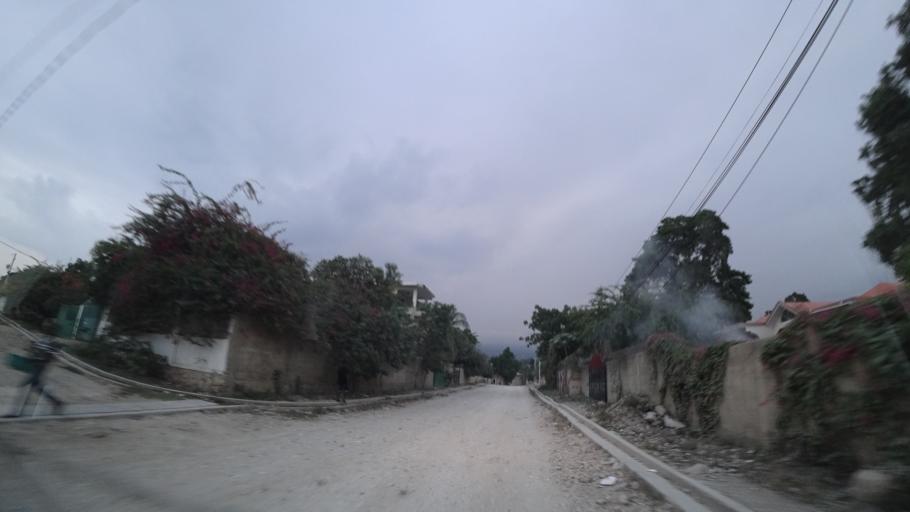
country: HT
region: Ouest
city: Delmas 73
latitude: 18.5471
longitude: -72.2870
